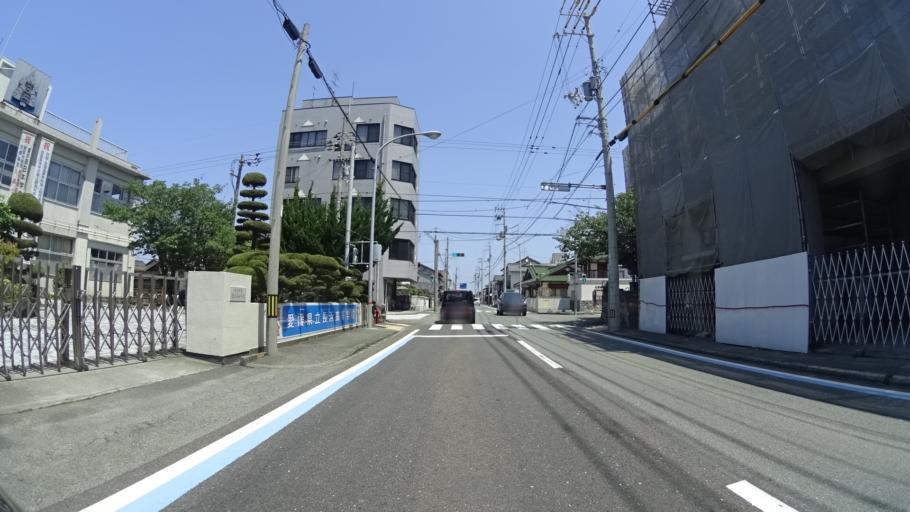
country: JP
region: Ehime
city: Ozu
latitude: 33.6145
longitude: 132.4801
